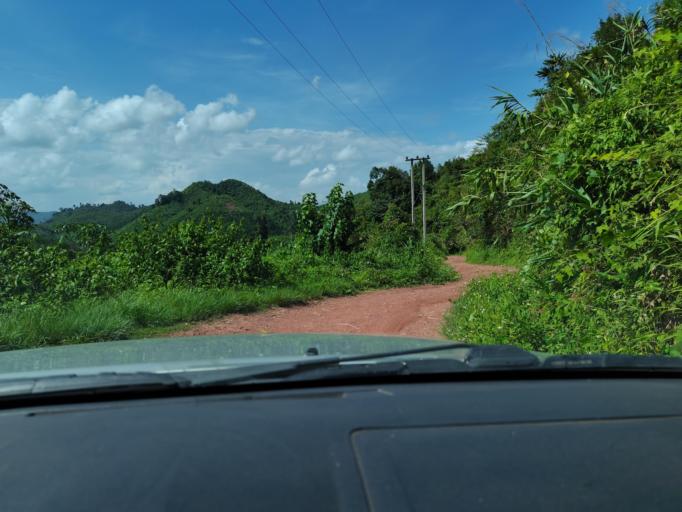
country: LA
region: Loungnamtha
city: Muang Nale
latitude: 20.5578
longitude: 101.0575
